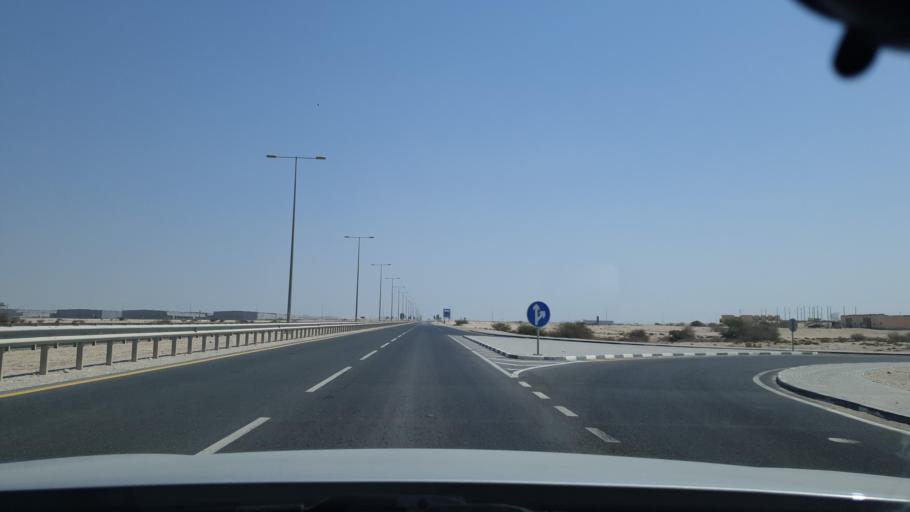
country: QA
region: Baladiyat Umm Salal
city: Umm Salal Muhammad
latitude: 25.3879
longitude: 51.3434
